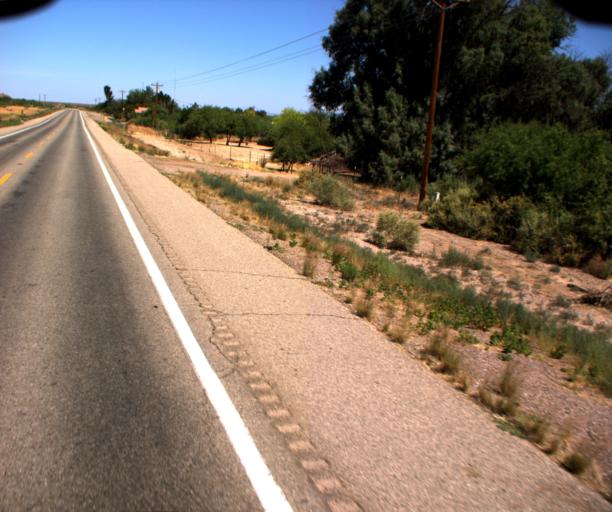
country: US
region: Arizona
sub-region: Graham County
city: Bylas
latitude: 33.0675
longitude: -110.0138
